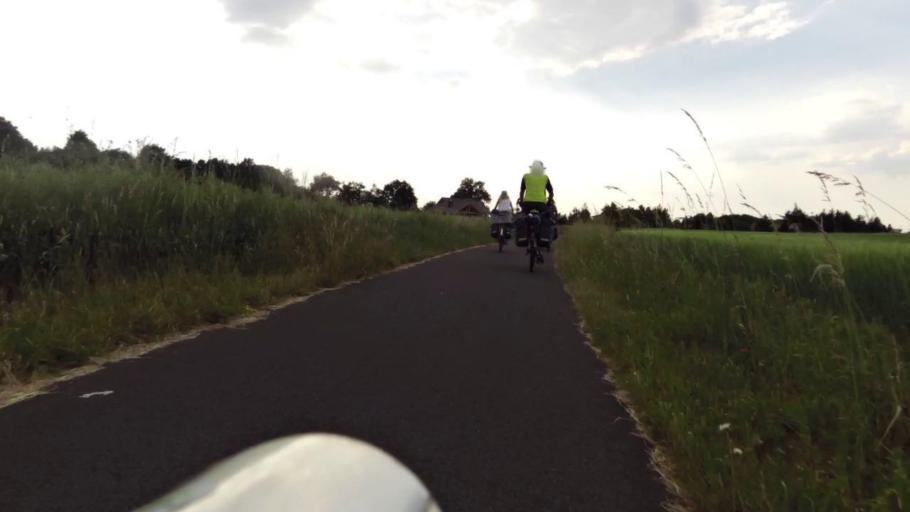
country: PL
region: Kujawsko-Pomorskie
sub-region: Powiat torunski
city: Lubianka
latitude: 53.1105
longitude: 18.4766
